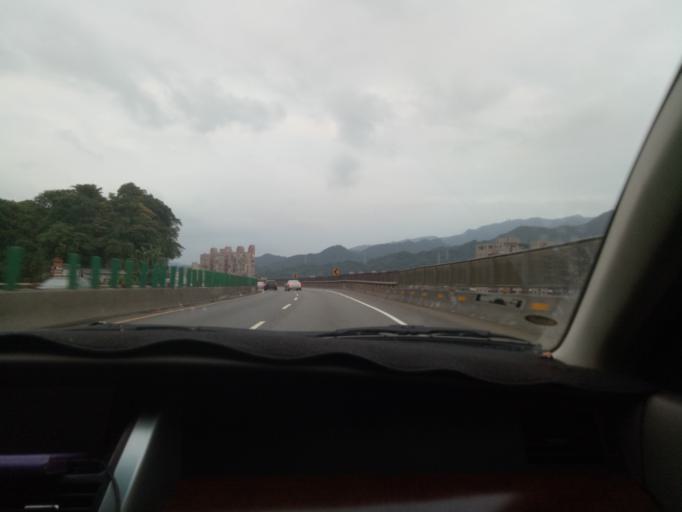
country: TW
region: Taiwan
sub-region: Keelung
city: Keelung
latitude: 25.1011
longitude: 121.7487
